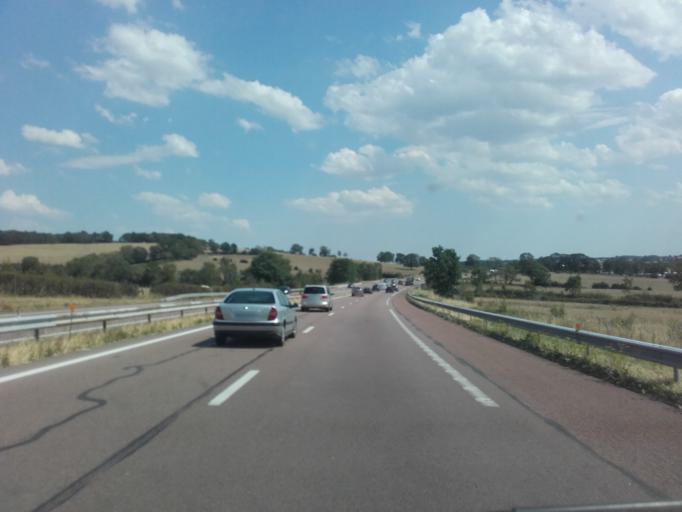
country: FR
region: Bourgogne
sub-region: Departement de l'Yonne
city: Avallon
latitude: 47.5503
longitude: 3.9617
